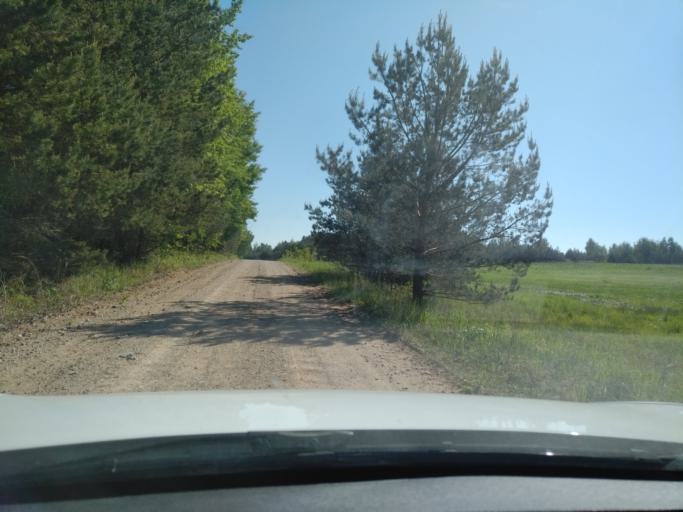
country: LT
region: Panevezys
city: Rokiskis
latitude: 55.7654
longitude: 25.6299
